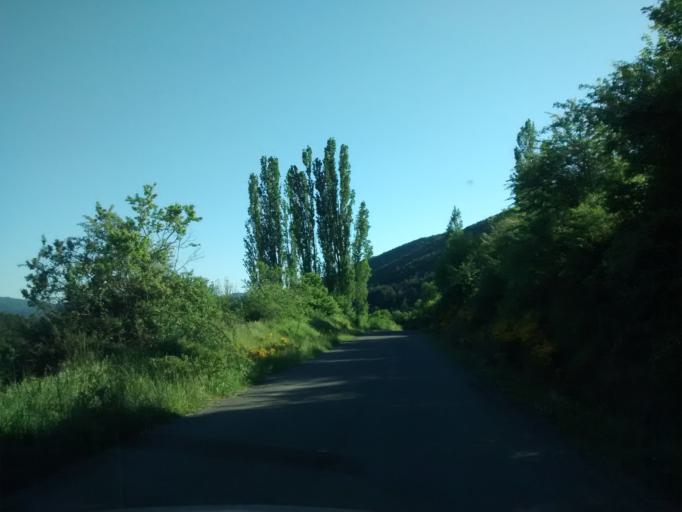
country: ES
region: Aragon
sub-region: Provincia de Huesca
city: Borau
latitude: 42.7033
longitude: -0.6144
